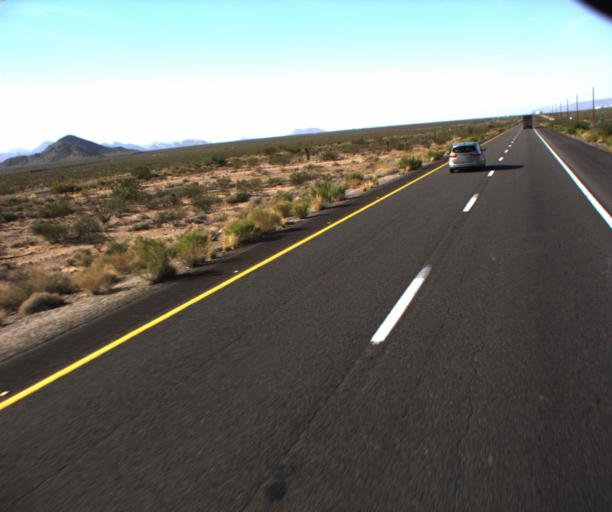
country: US
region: Arizona
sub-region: Mohave County
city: Kingman
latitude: 35.0913
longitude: -114.1200
